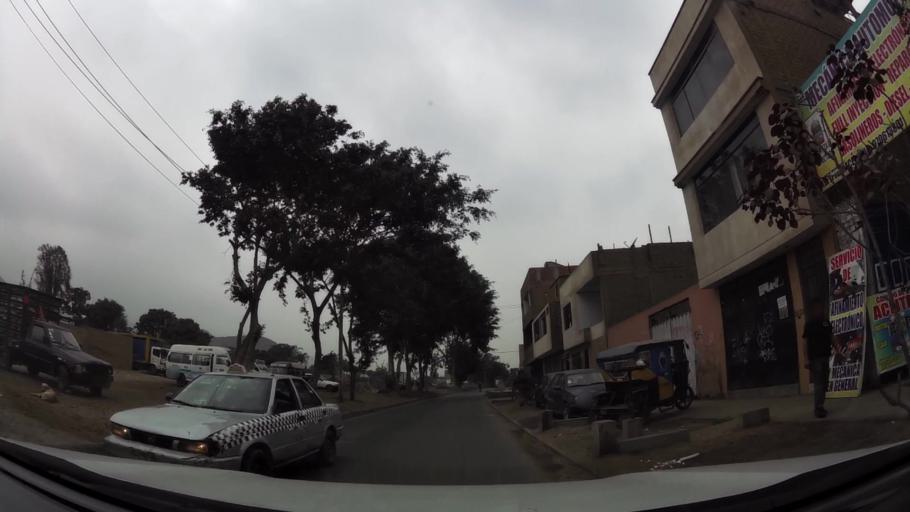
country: PE
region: Lima
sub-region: Lima
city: Independencia
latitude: -11.9357
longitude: -77.0821
